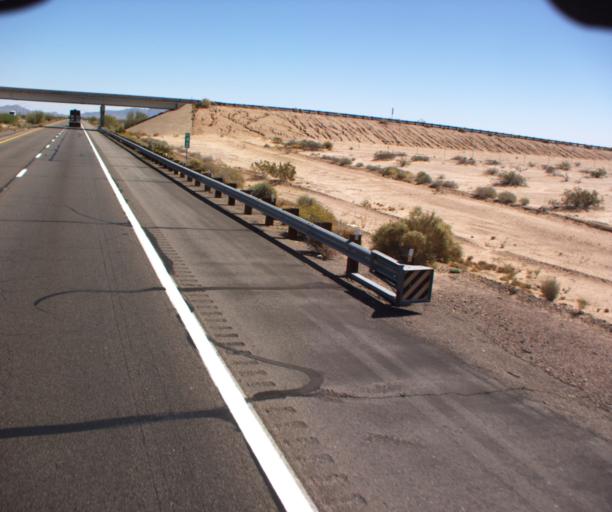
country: US
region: Arizona
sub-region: Yuma County
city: Wellton
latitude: 32.6932
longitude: -113.9546
